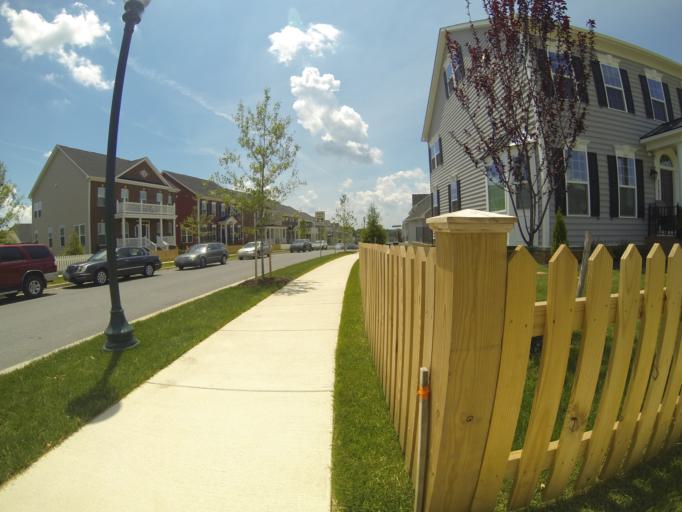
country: US
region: Maryland
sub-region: Montgomery County
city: Clarksburg
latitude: 39.2267
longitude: -77.2413
